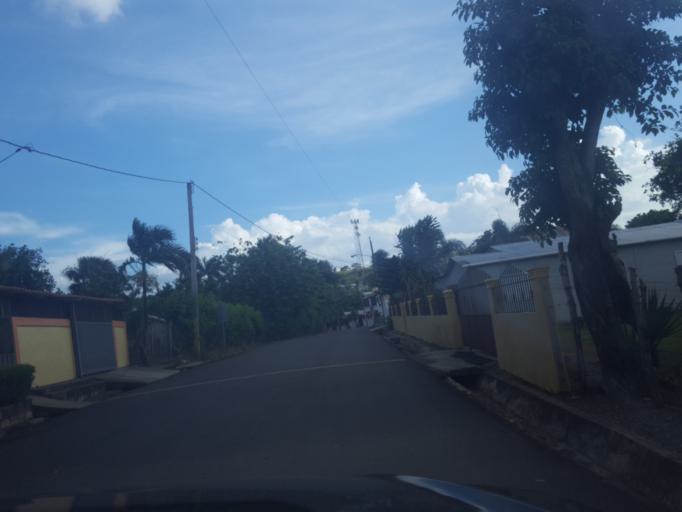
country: DO
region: Santiago
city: Baitoa
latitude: 19.3602
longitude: -70.6331
